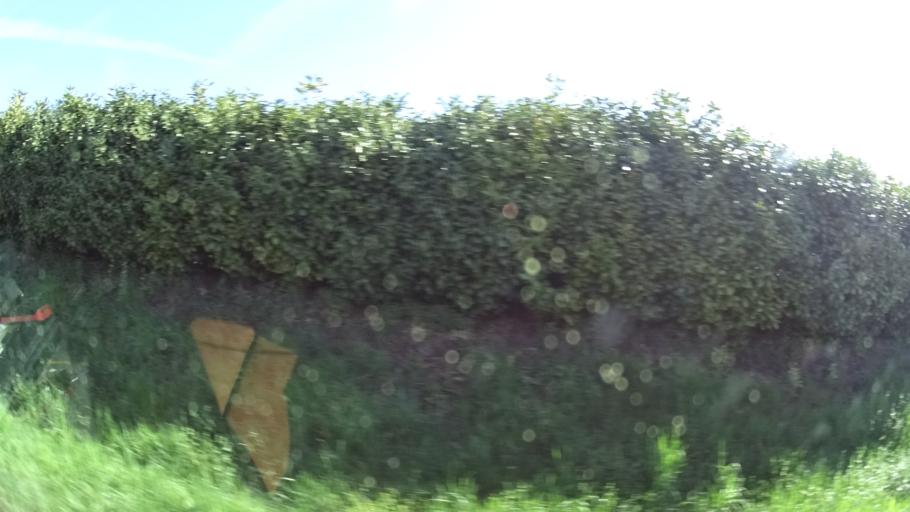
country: DE
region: Baden-Wuerttemberg
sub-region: Karlsruhe Region
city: Altensteig
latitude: 48.6229
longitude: 8.6422
